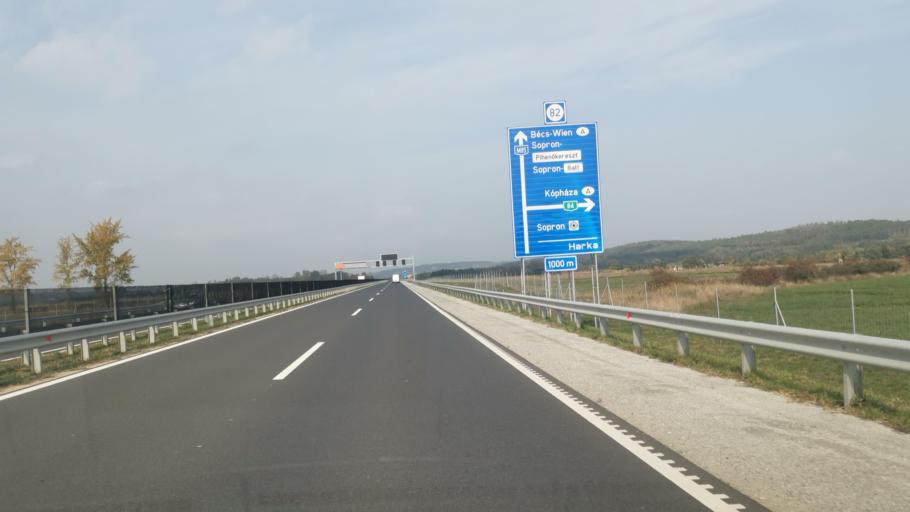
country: AT
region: Burgenland
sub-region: Politischer Bezirk Oberpullendorf
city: Deutschkreutz
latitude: 47.6412
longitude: 16.6280
